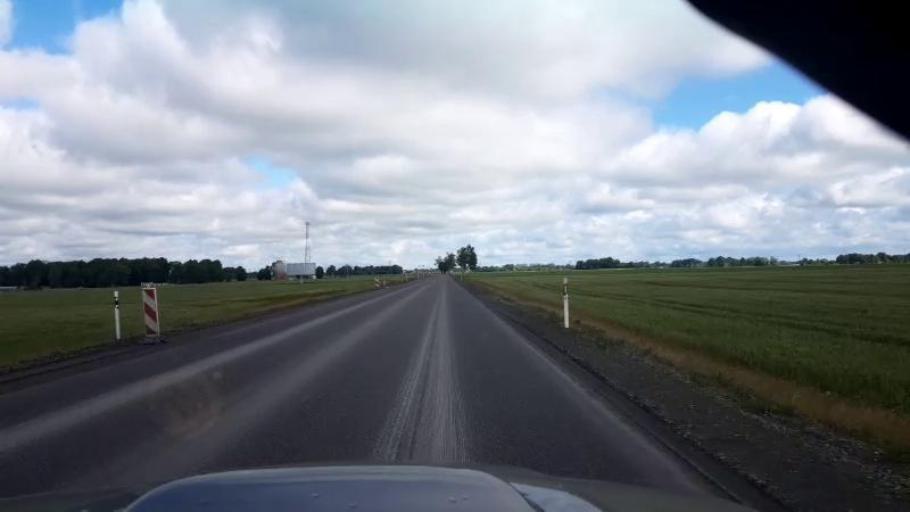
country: LV
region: Bauskas Rajons
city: Bauska
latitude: 56.2867
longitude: 24.3575
